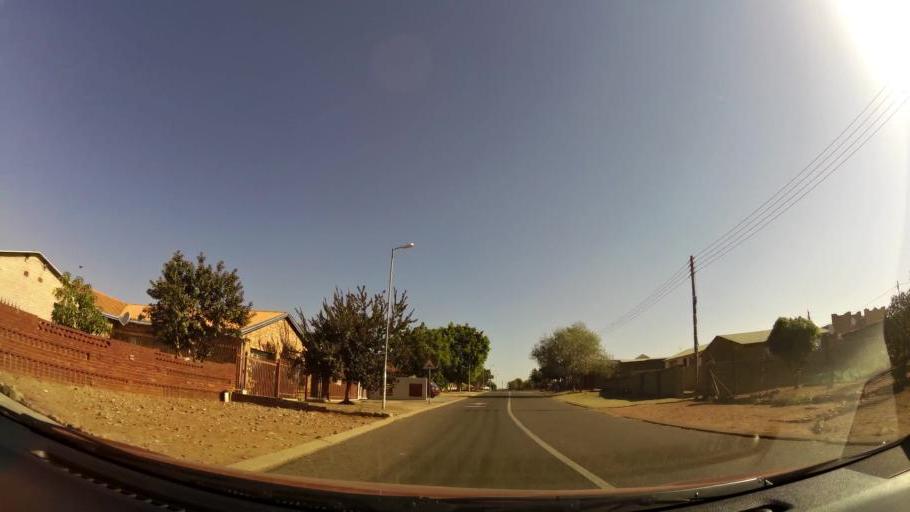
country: ZA
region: Gauteng
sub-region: City of Tshwane Metropolitan Municipality
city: Mabopane
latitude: -25.5286
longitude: 28.1024
